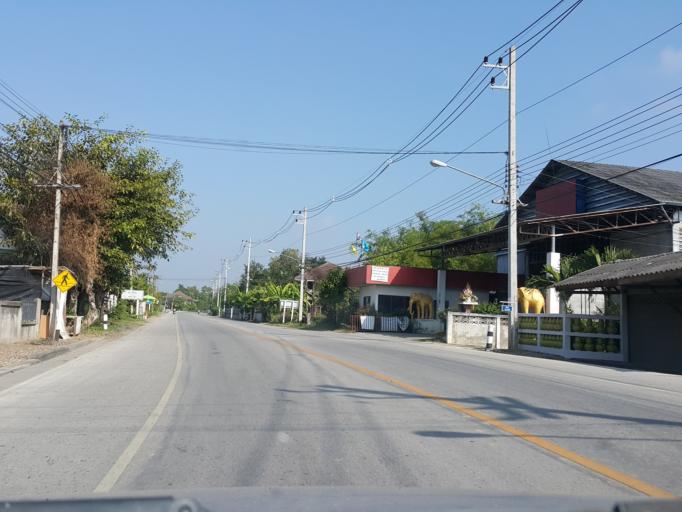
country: TH
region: Chiang Mai
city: San Sai
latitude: 18.8481
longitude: 99.1316
